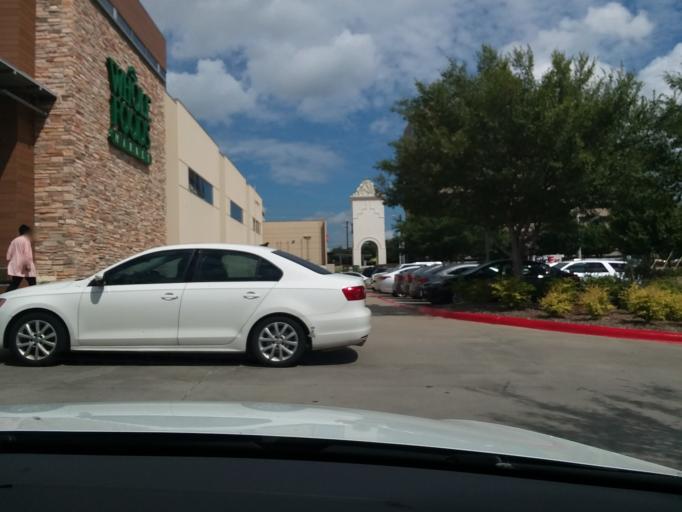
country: US
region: Texas
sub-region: Dallas County
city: Addison
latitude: 32.9529
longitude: -96.8208
